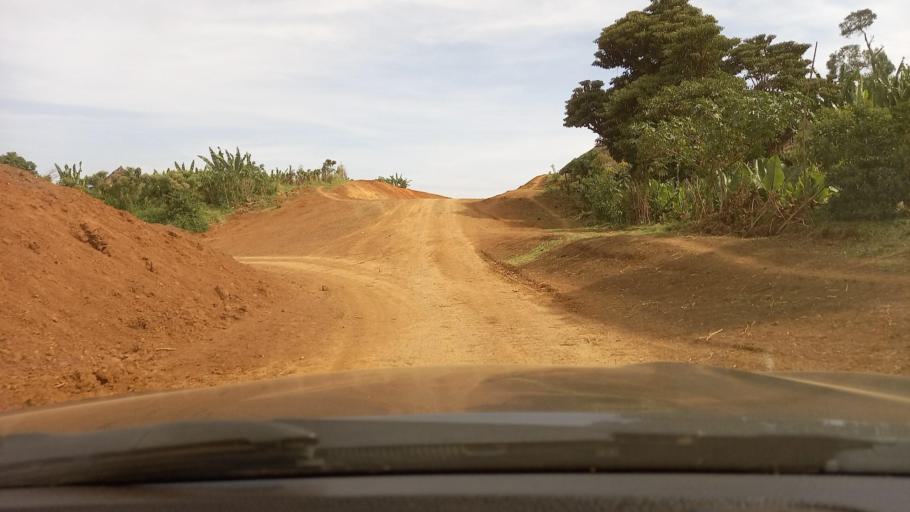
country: ET
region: Southern Nations, Nationalities, and People's Region
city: Mizan Teferi
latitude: 6.1685
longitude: 35.7390
